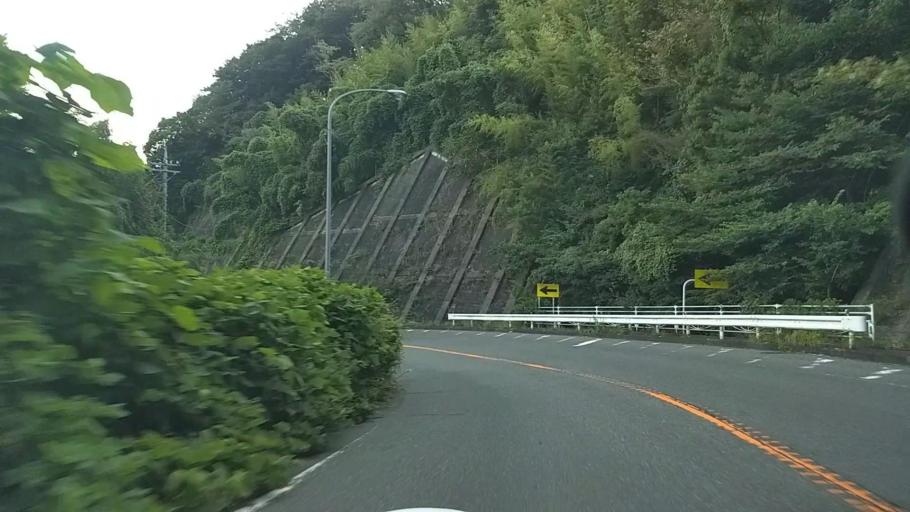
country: JP
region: Shizuoka
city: Fujinomiya
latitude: 35.3181
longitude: 138.4392
